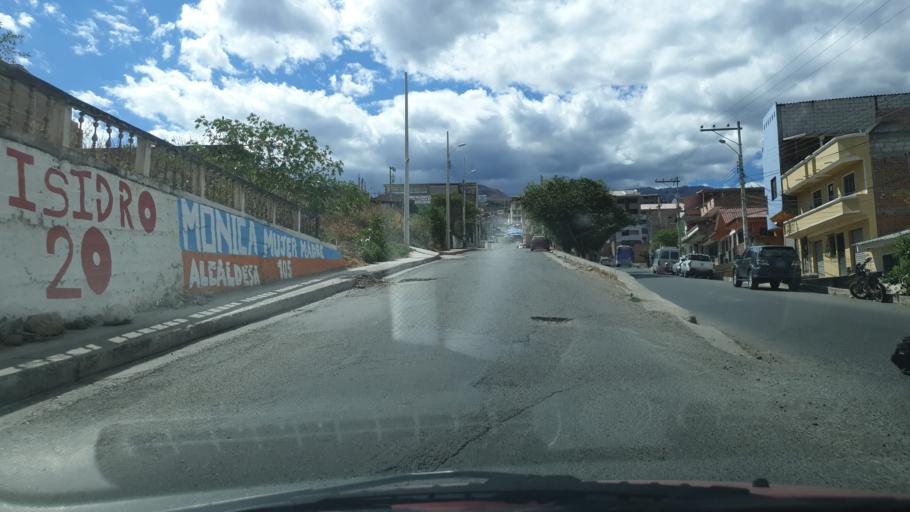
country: EC
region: Azuay
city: Cuenca
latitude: -3.2780
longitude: -79.3138
